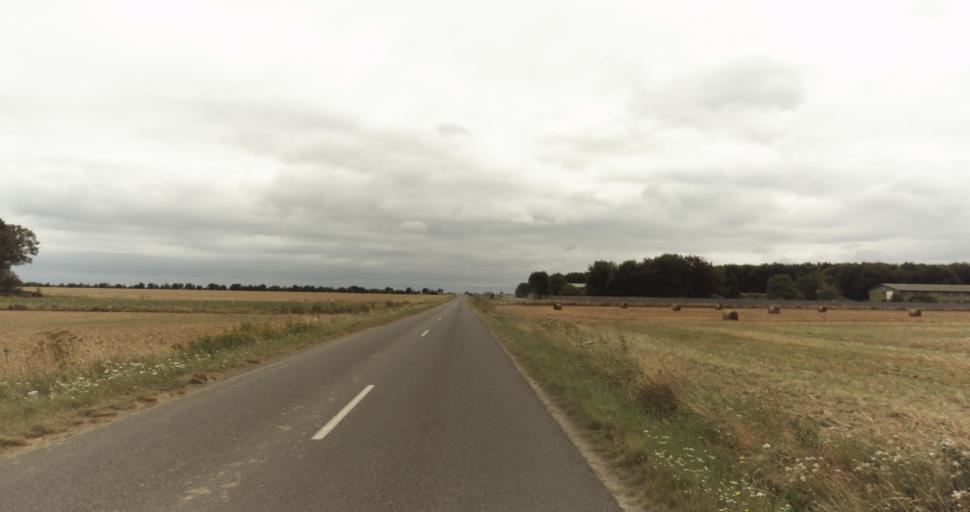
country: FR
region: Haute-Normandie
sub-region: Departement de l'Eure
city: Gravigny
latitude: 49.0476
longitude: 1.2296
